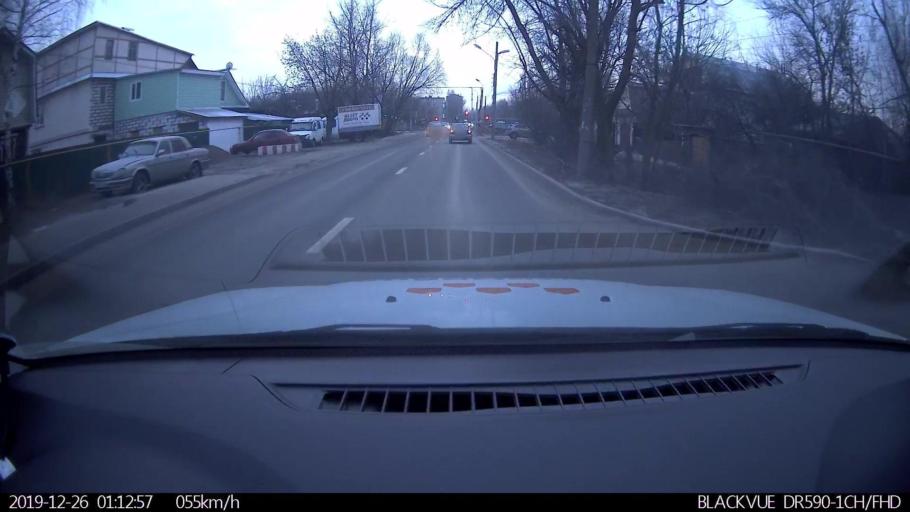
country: RU
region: Nizjnij Novgorod
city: Nizhniy Novgorod
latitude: 56.2806
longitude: 43.9131
